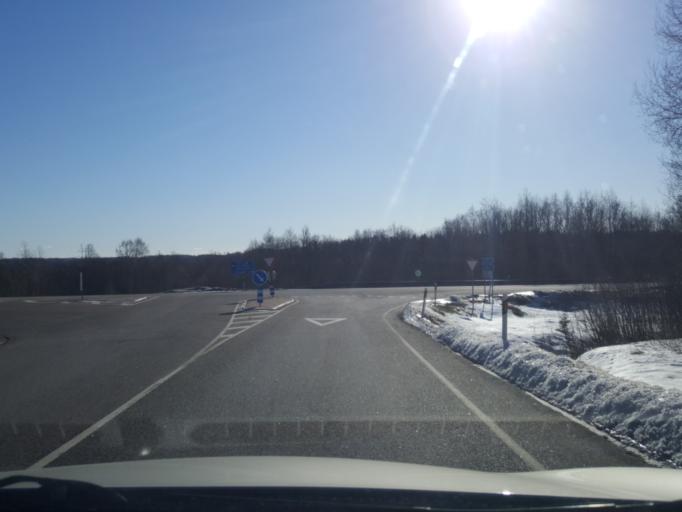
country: EE
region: Viljandimaa
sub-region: Viiratsi vald
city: Viiratsi
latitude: 58.4079
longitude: 25.6672
